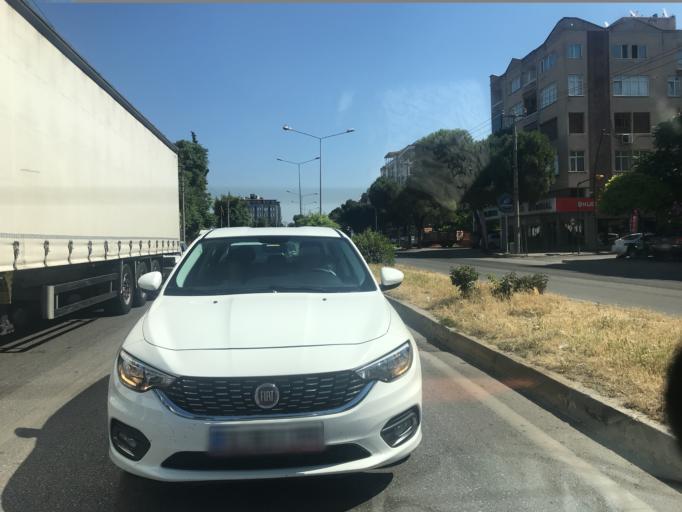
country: TR
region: Manisa
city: Akhisar
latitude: 38.9208
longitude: 27.8334
